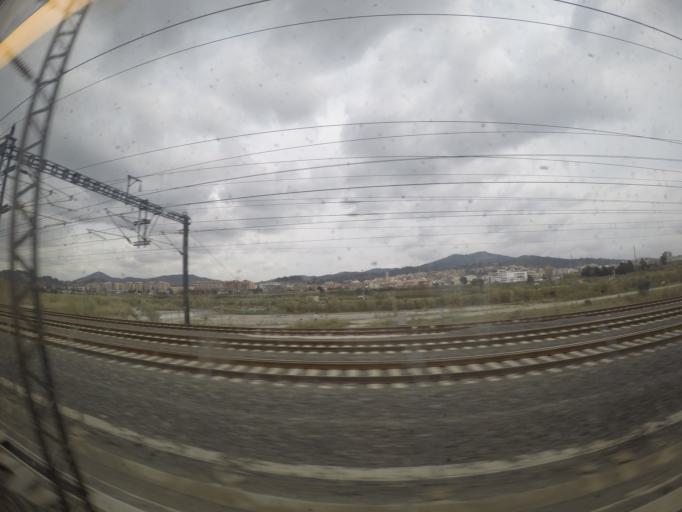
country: ES
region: Catalonia
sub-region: Provincia de Barcelona
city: Molins de Rei
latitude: 41.4104
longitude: 2.0091
